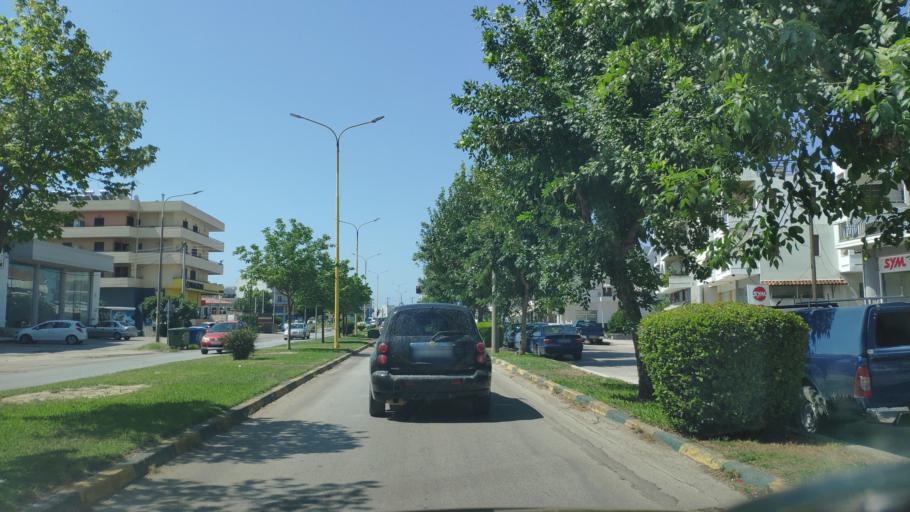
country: GR
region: Epirus
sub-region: Nomos Artas
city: Arta
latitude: 39.1551
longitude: 20.9785
